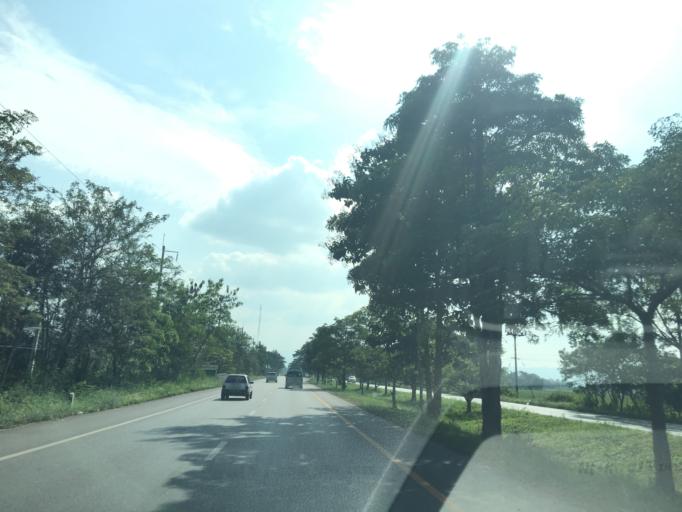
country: TH
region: Chiang Rai
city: Mae Lao
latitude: 19.7365
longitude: 99.7214
